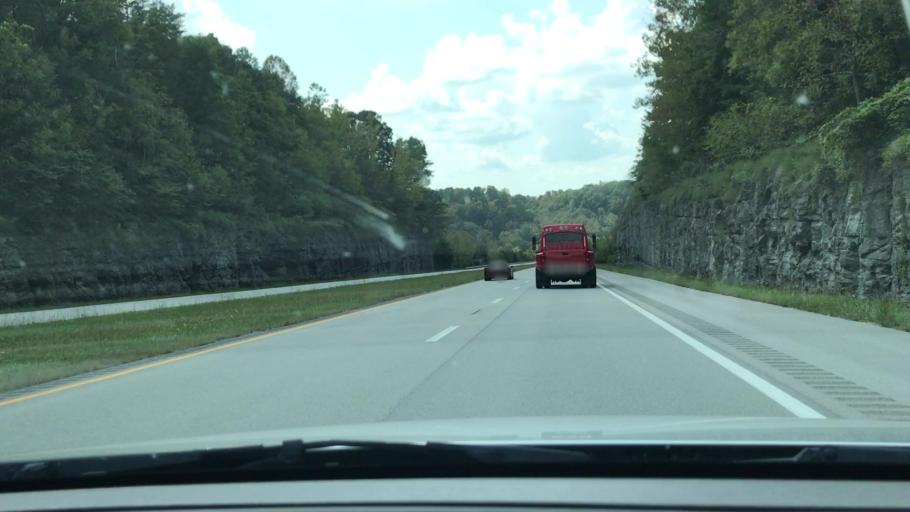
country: US
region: Kentucky
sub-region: Russell County
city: Russell Springs
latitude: 37.0902
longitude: -84.8820
